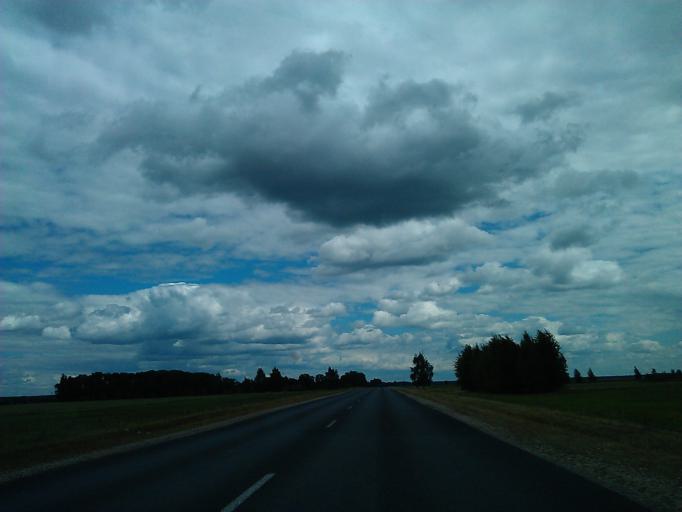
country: LV
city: Tervete
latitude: 56.6218
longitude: 23.4674
